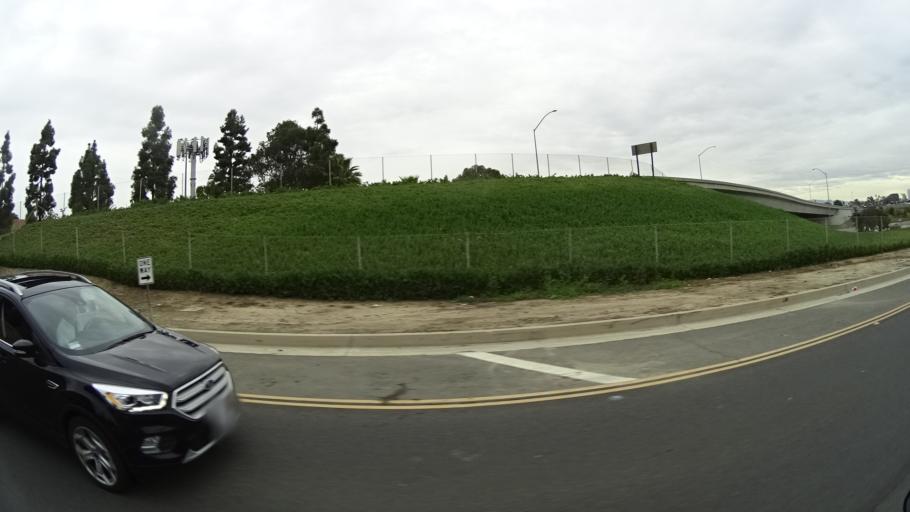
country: US
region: California
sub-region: Orange County
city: Costa Mesa
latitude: 33.6654
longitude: -117.8807
